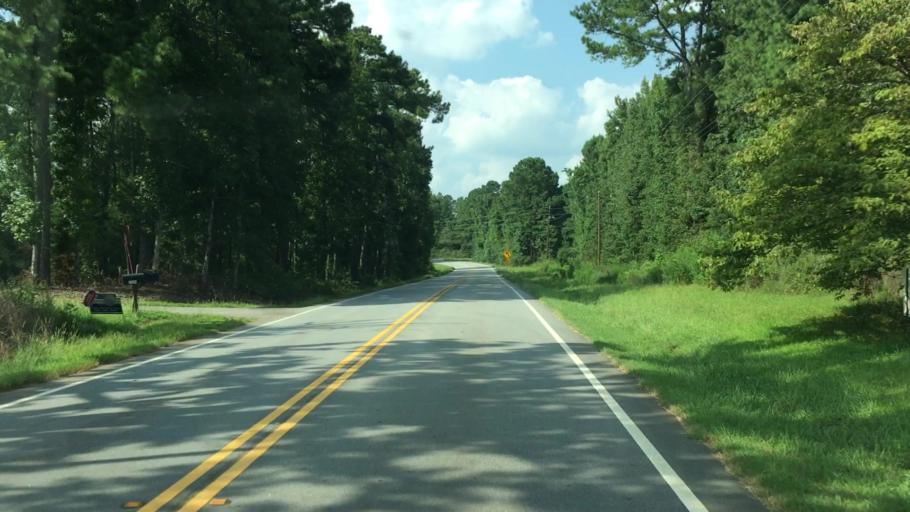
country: US
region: Georgia
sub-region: Jasper County
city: Monticello
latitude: 33.4037
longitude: -83.7581
